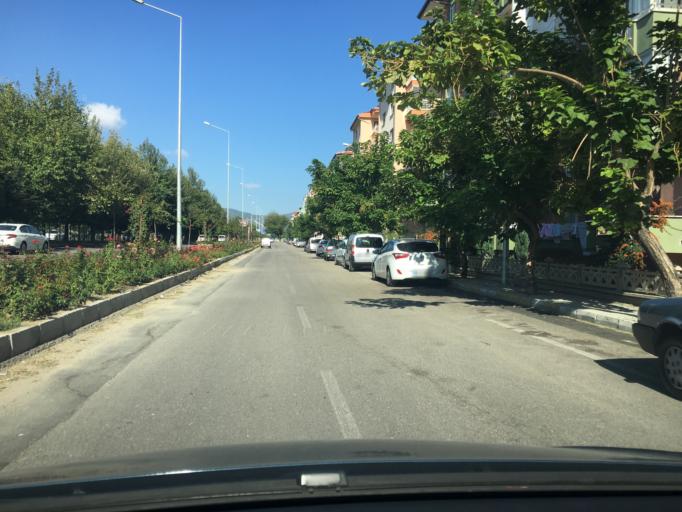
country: TR
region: Isparta
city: Isparta
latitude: 37.7893
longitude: 30.5519
